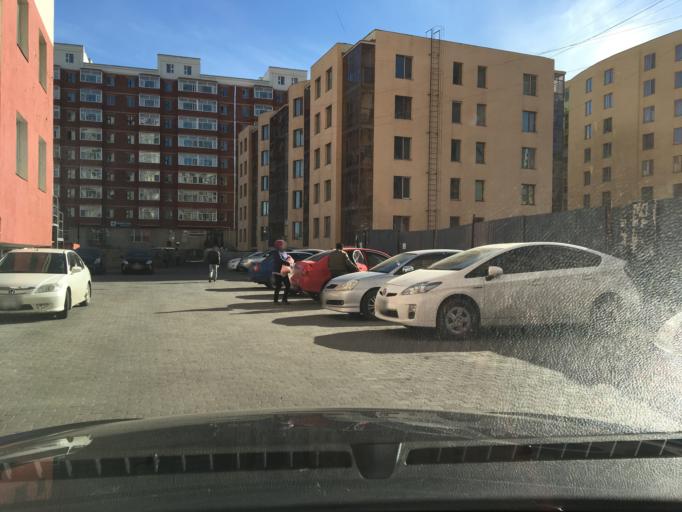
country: MN
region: Ulaanbaatar
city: Ulaanbaatar
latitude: 47.8917
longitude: 106.8950
